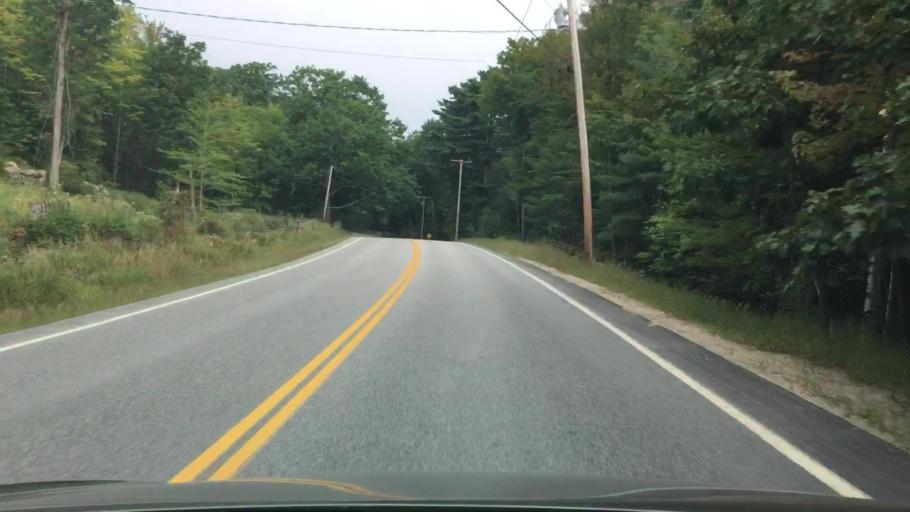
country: US
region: Maine
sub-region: Oxford County
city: Hartford
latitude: 44.3479
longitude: -70.2994
